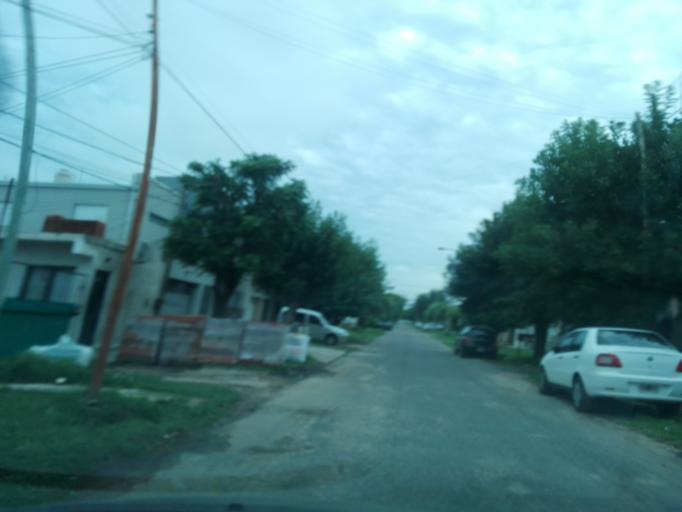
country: AR
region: Buenos Aires
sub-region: Partido de La Plata
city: La Plata
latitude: -34.9393
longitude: -57.9816
